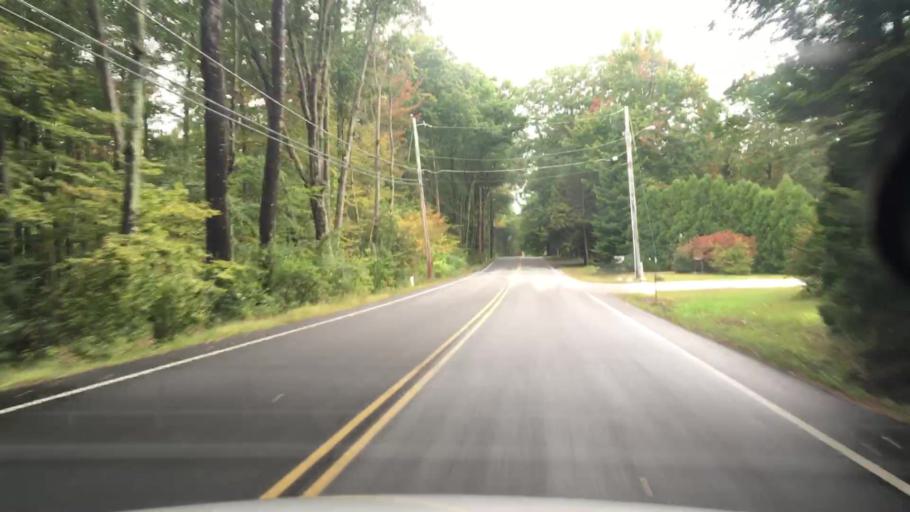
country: US
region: New Hampshire
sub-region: Strafford County
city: Rochester
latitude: 43.2837
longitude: -70.9565
